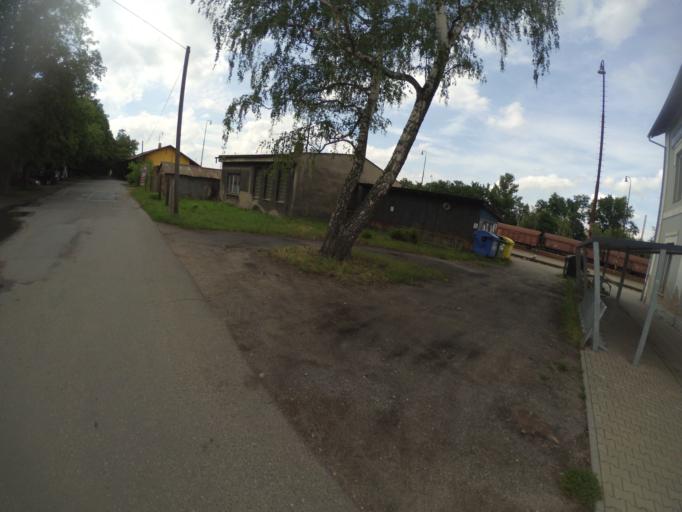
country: CZ
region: Central Bohemia
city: Neratovice
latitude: 50.2624
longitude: 14.5170
